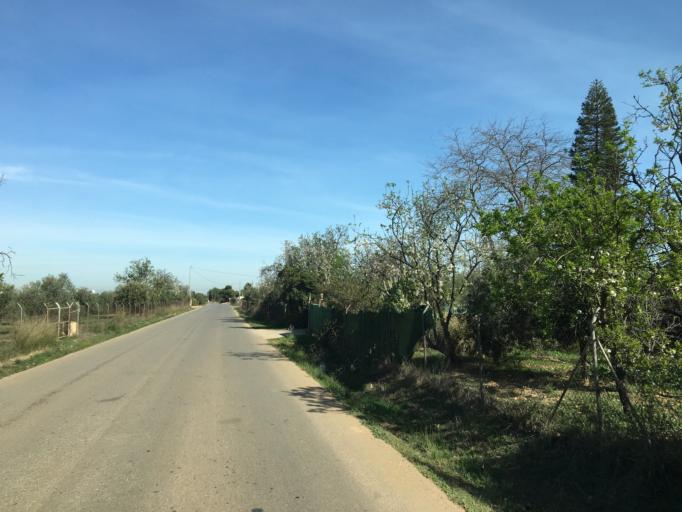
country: ES
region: Murcia
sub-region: Murcia
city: Cartagena
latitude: 37.6519
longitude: -1.0245
